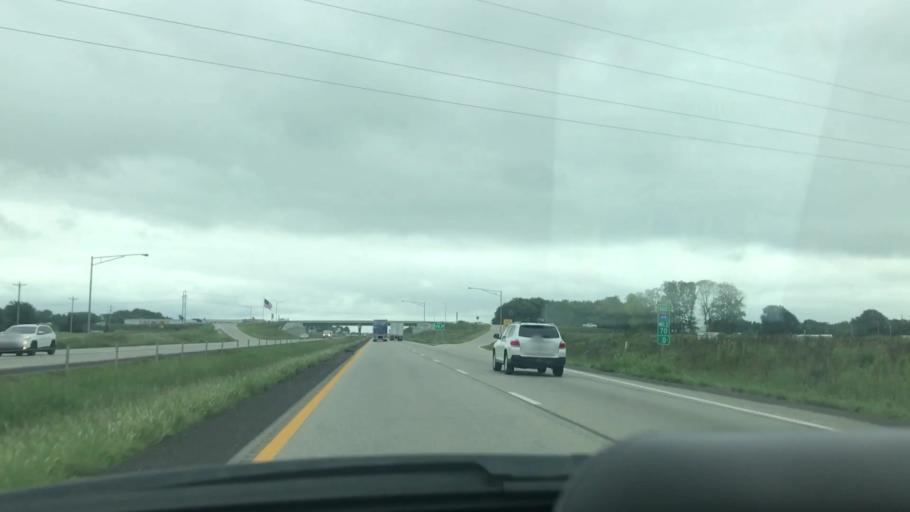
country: US
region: Missouri
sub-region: Greene County
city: Republic
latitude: 37.1997
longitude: -93.4271
